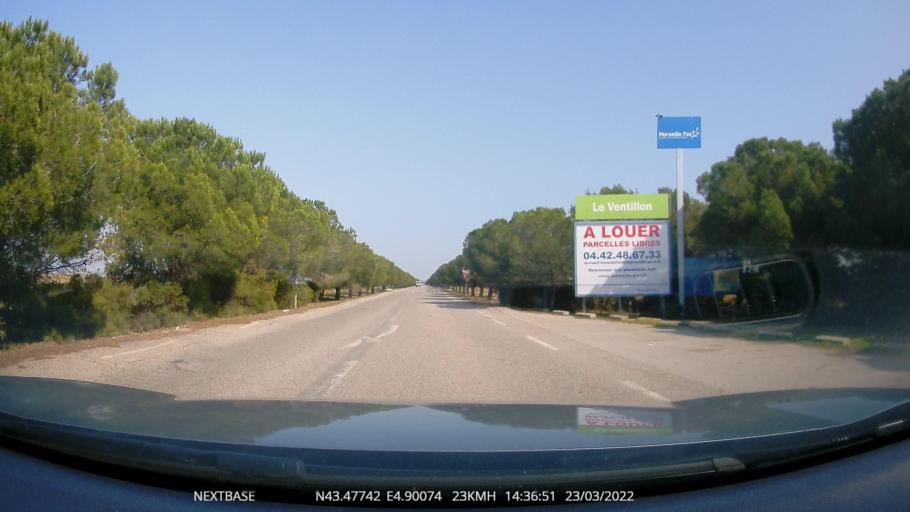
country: FR
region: Provence-Alpes-Cote d'Azur
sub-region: Departement des Bouches-du-Rhone
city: Fos-sur-Mer
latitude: 43.4774
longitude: 4.9009
